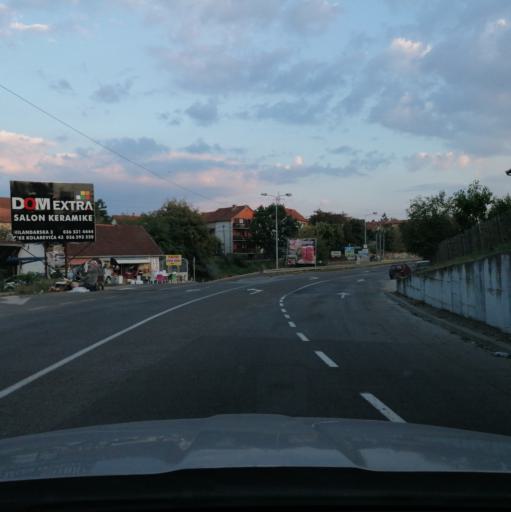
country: RS
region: Central Serbia
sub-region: Raski Okrug
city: Kraljevo
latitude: 43.7358
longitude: 20.6798
